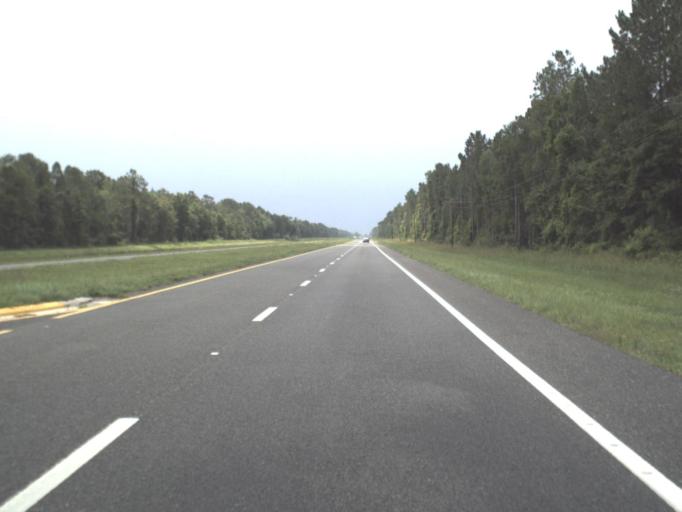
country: US
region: Florida
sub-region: Levy County
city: Chiefland
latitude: 29.3557
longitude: -82.7859
